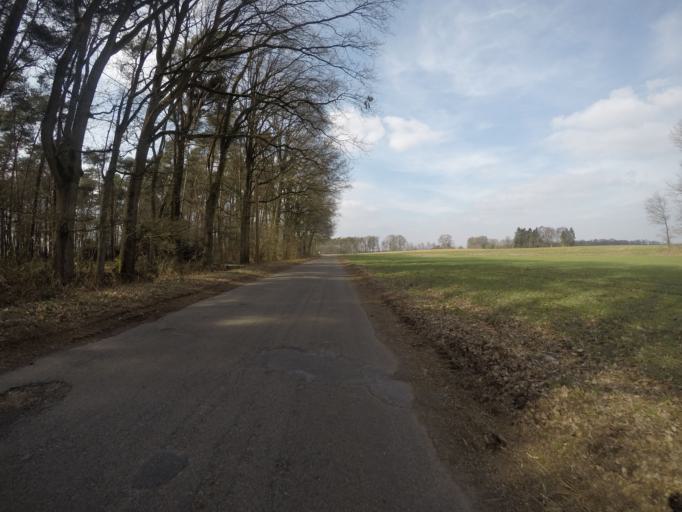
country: DE
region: North Rhine-Westphalia
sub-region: Regierungsbezirk Munster
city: Rhede
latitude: 51.8058
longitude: 6.7125
